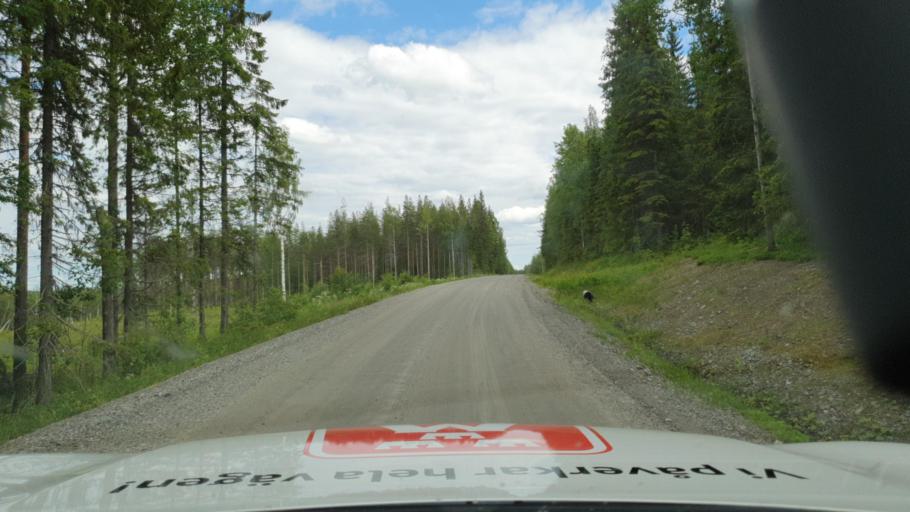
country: SE
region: Vaesterbotten
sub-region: Norsjo Kommun
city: Norsjoe
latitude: 64.8074
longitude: 19.6135
